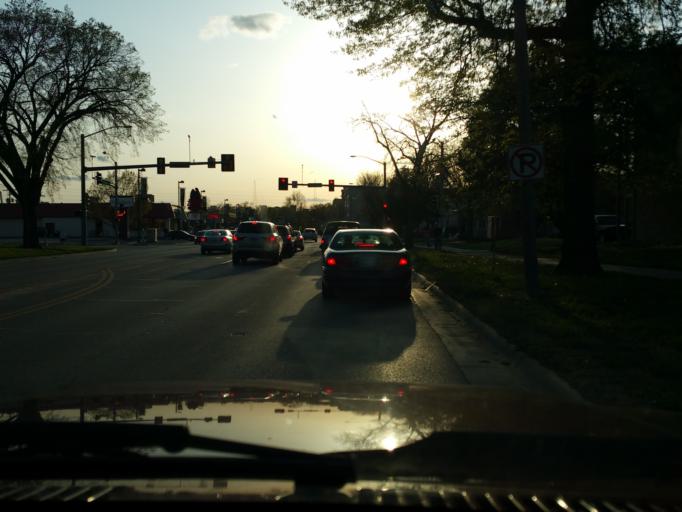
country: US
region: Kansas
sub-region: Riley County
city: Manhattan
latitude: 39.1868
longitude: -96.5724
